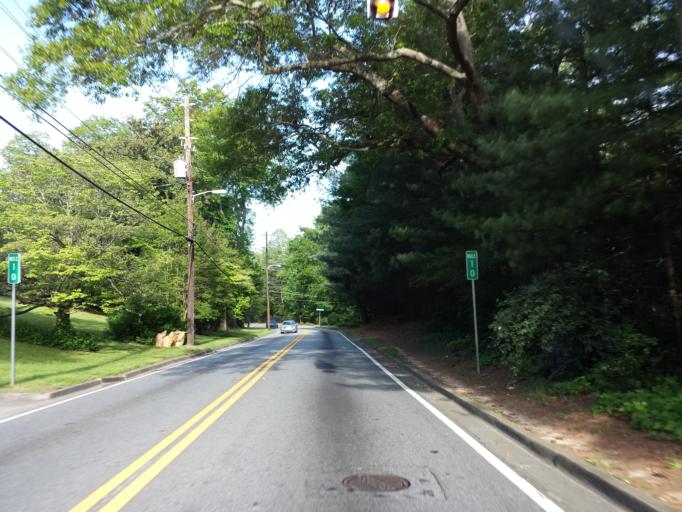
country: US
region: Georgia
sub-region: Cobb County
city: Marietta
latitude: 33.9517
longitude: -84.5590
